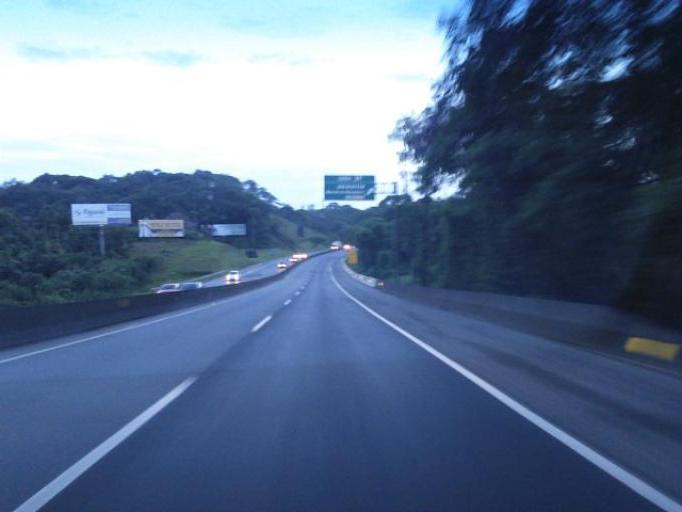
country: BR
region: Santa Catarina
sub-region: Joinville
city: Joinville
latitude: -26.2878
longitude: -48.8864
